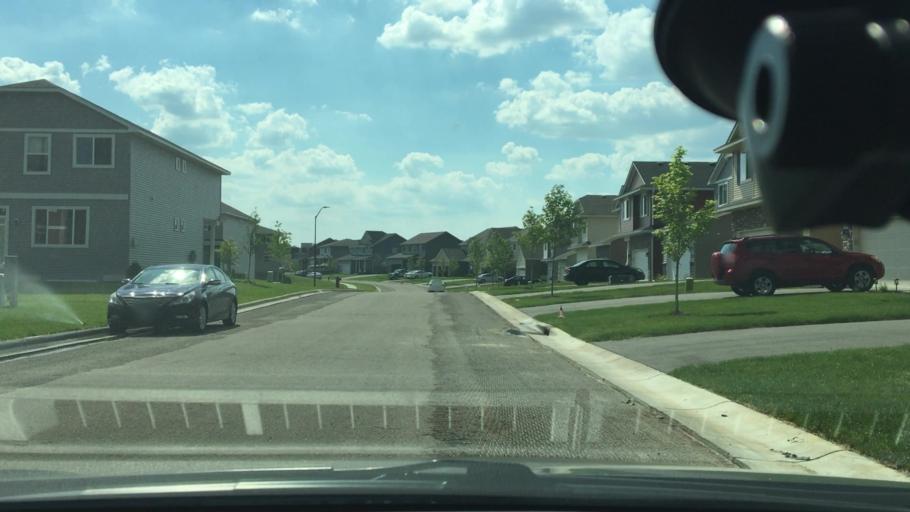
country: US
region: Minnesota
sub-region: Hennepin County
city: New Hope
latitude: 45.0540
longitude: -93.3809
